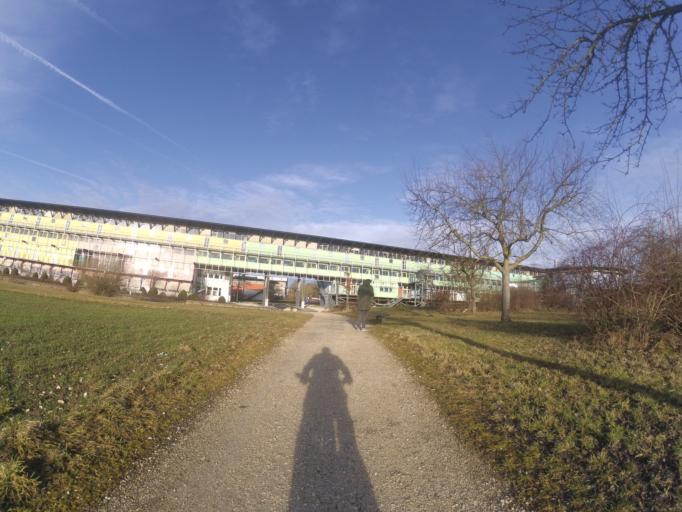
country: DE
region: Baden-Wuerttemberg
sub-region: Tuebingen Region
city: Dornstadt
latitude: 48.4188
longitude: 9.9464
